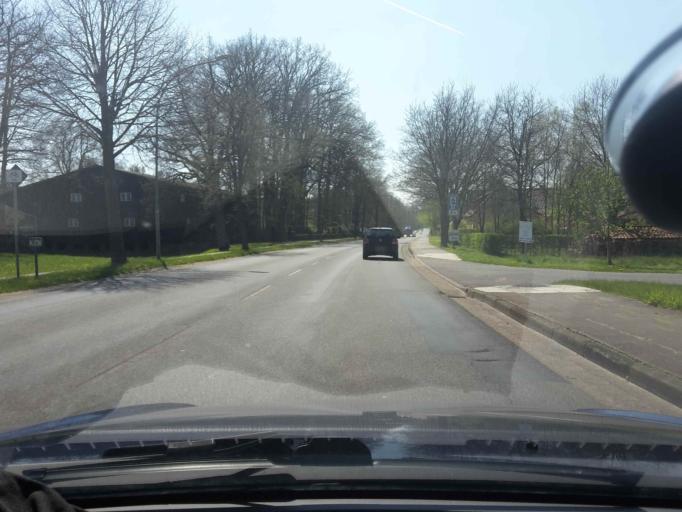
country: DE
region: Lower Saxony
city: Schneverdingen
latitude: 53.0732
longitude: 9.8633
